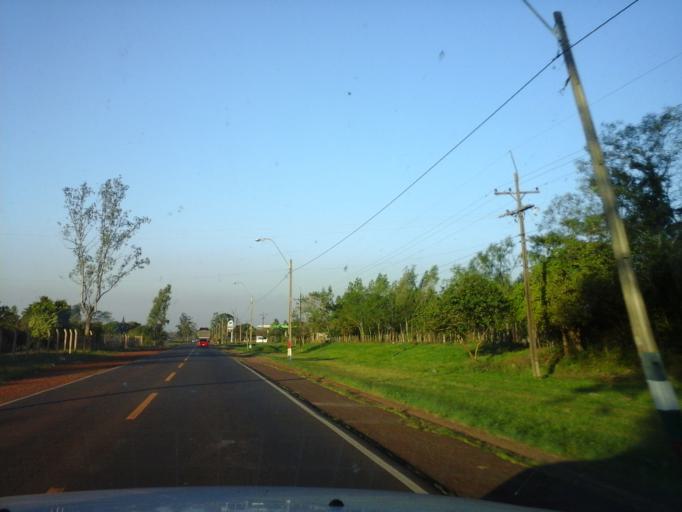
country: PY
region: Itapua
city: General Delgado
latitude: -27.0897
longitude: -56.5122
